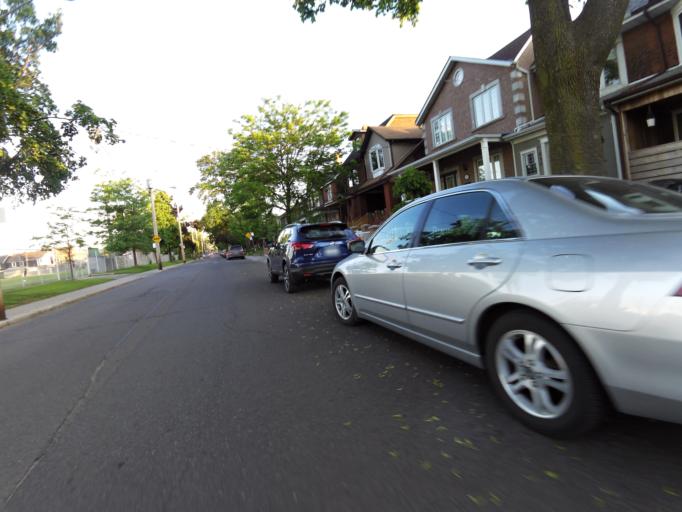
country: CA
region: Ontario
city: Toronto
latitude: 43.6571
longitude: -79.4384
